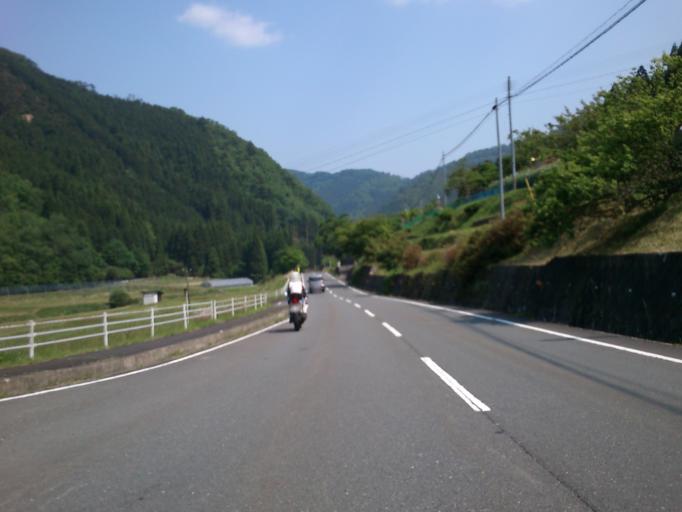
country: JP
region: Kyoto
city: Kameoka
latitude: 35.2403
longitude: 135.5611
